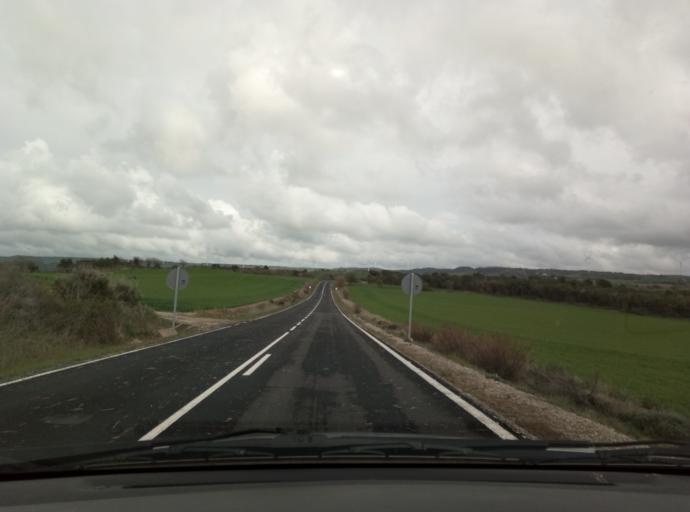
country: ES
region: Catalonia
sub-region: Provincia de Tarragona
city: Santa Coloma de Queralt
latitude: 41.5720
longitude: 1.3414
